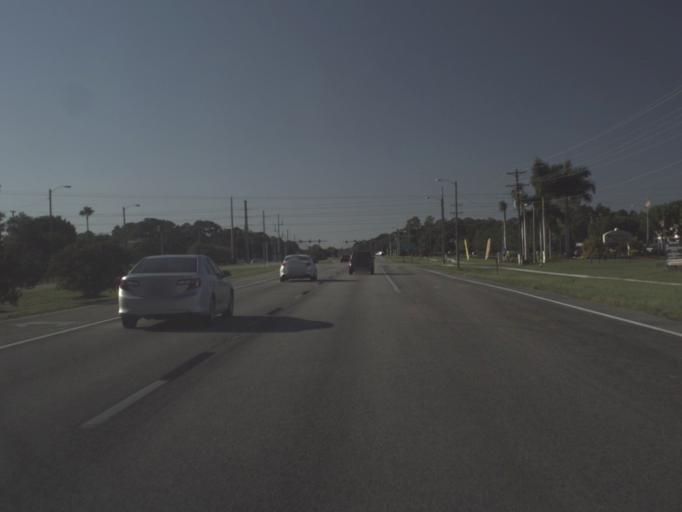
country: US
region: Florida
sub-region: Lee County
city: Palmona Park
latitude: 26.7002
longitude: -81.9005
